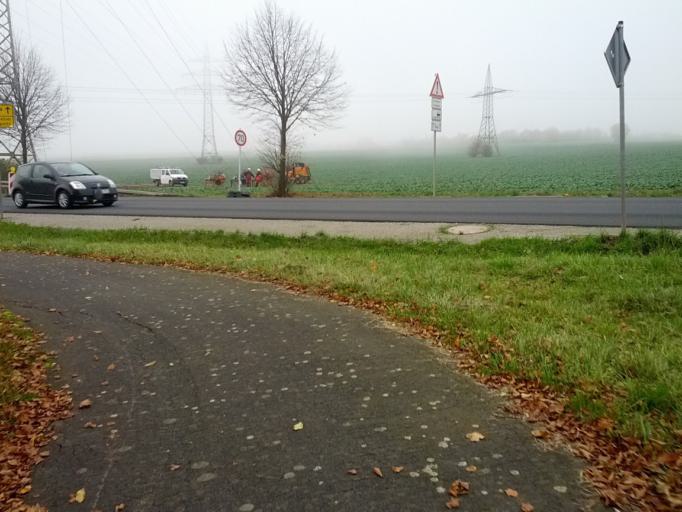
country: DE
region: Thuringia
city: Bischofroda
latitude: 50.9974
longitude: 10.3914
